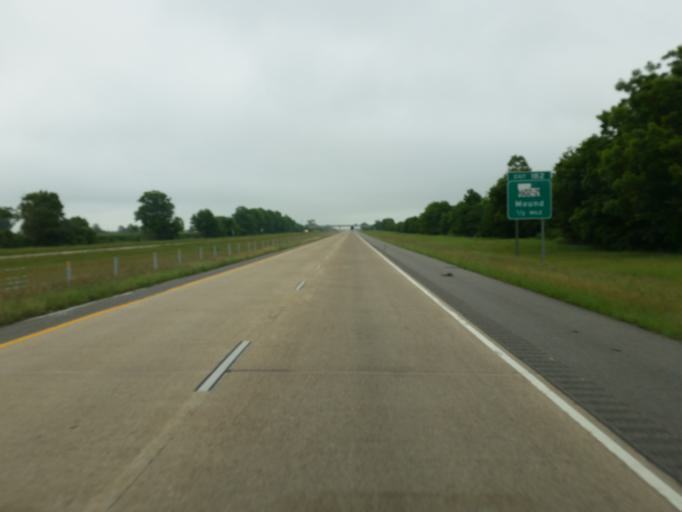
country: US
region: Mississippi
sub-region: Warren County
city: Vicksburg
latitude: 32.3313
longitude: -91.0338
